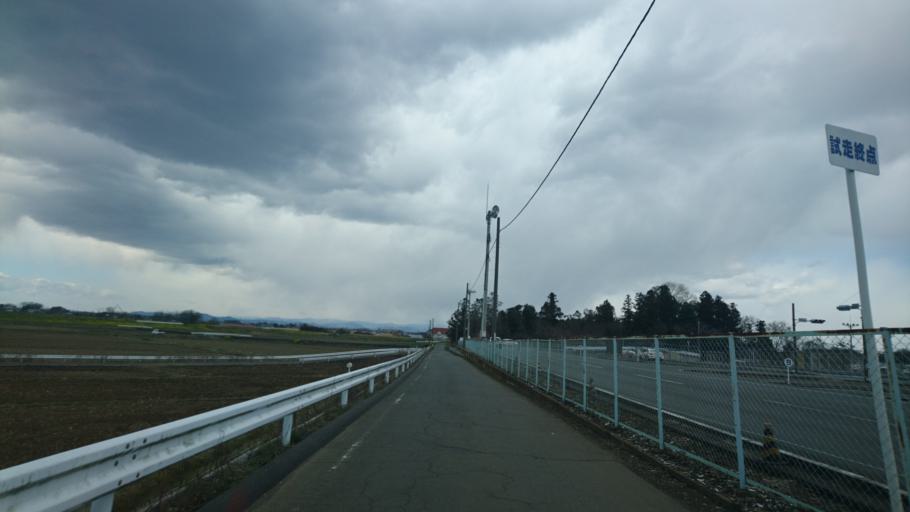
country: JP
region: Ibaraki
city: Yuki
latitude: 36.2693
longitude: 139.9113
